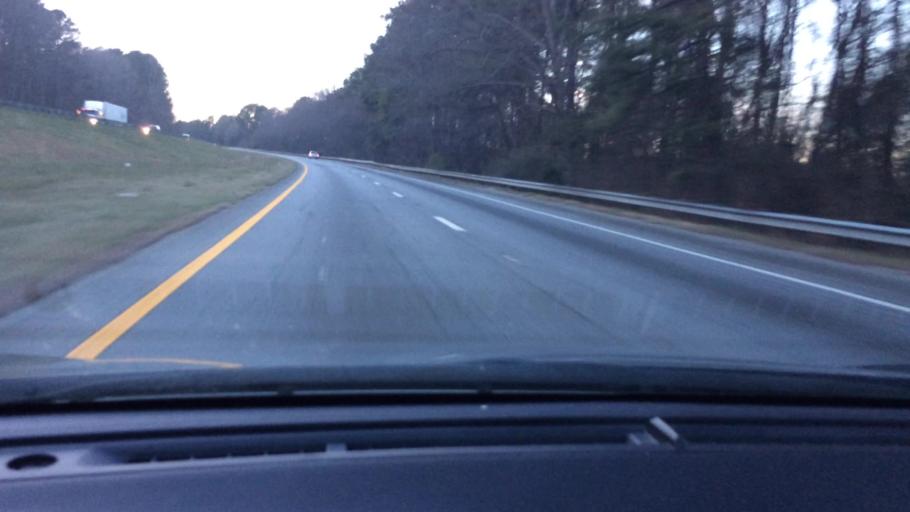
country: US
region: South Carolina
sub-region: Laurens County
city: Joanna
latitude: 34.4245
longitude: -81.7201
